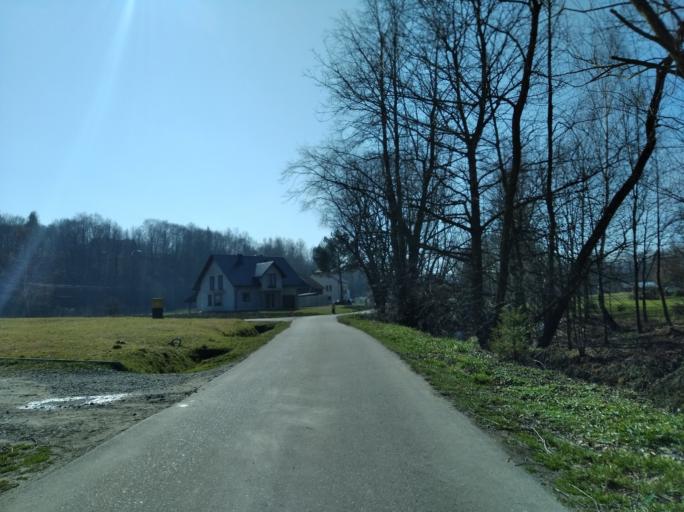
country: PL
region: Subcarpathian Voivodeship
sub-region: Powiat strzyzowski
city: Wysoka Strzyzowska
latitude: 49.8558
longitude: 21.7373
